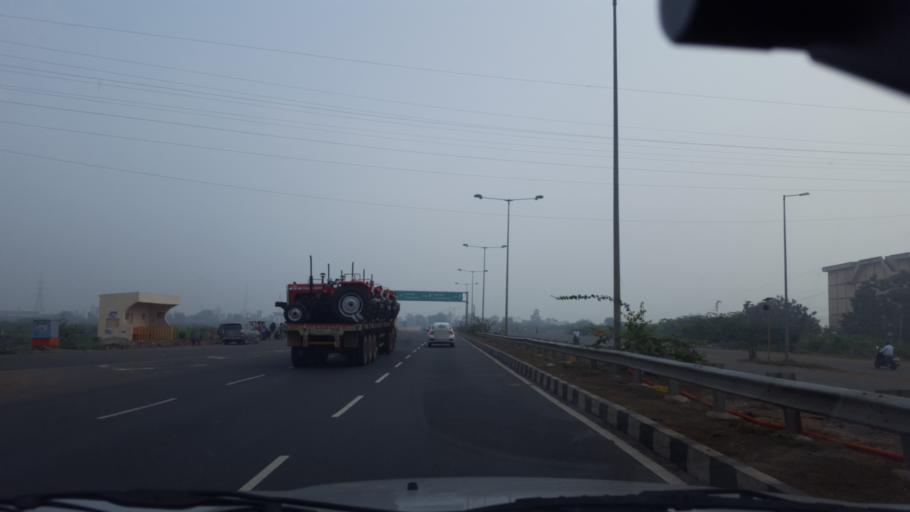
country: IN
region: Andhra Pradesh
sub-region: Prakasam
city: Ongole
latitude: 15.5463
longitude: 80.0537
